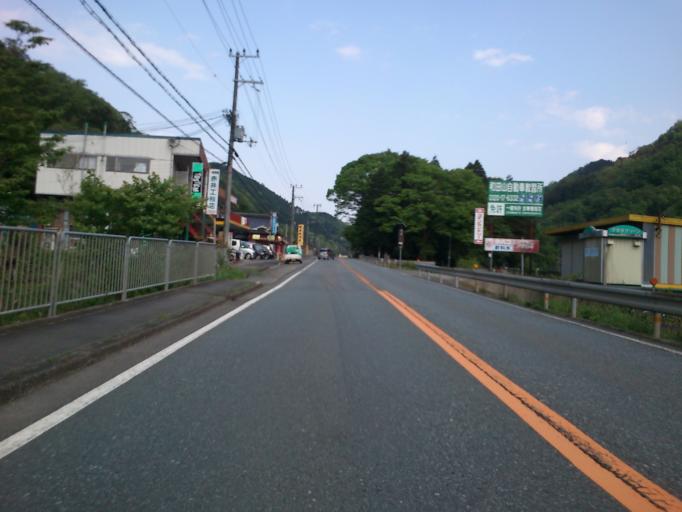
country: JP
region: Kyoto
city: Fukuchiyama
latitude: 35.3243
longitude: 134.9694
